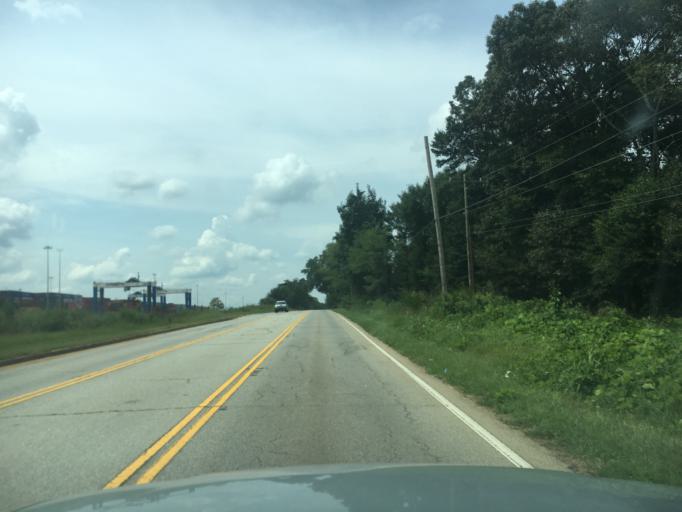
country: US
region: South Carolina
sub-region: Greenville County
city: Greer
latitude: 34.9351
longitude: -82.1953
